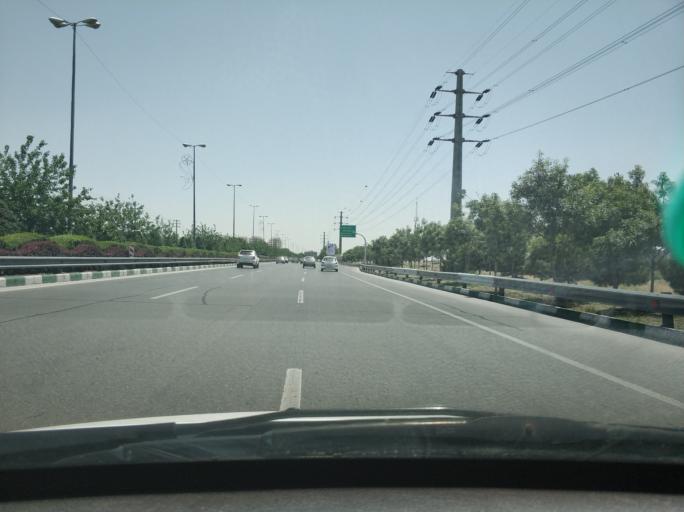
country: IR
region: Razavi Khorasan
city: Mashhad
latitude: 36.3466
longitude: 59.4840
